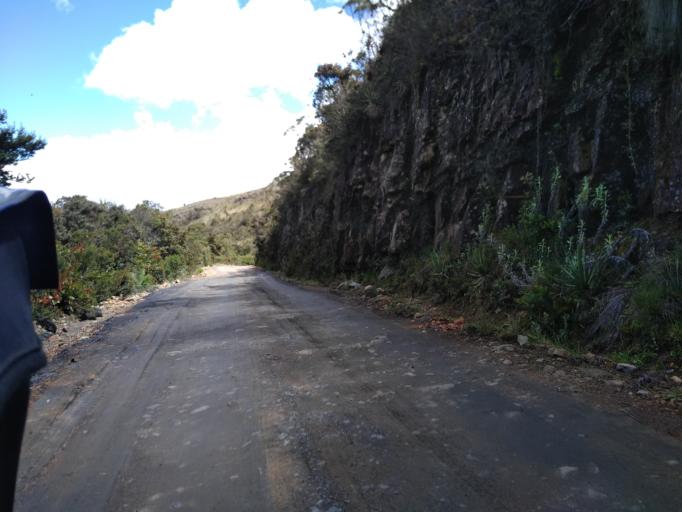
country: CO
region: Boyaca
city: Duitama
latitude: 5.9367
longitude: -73.0978
